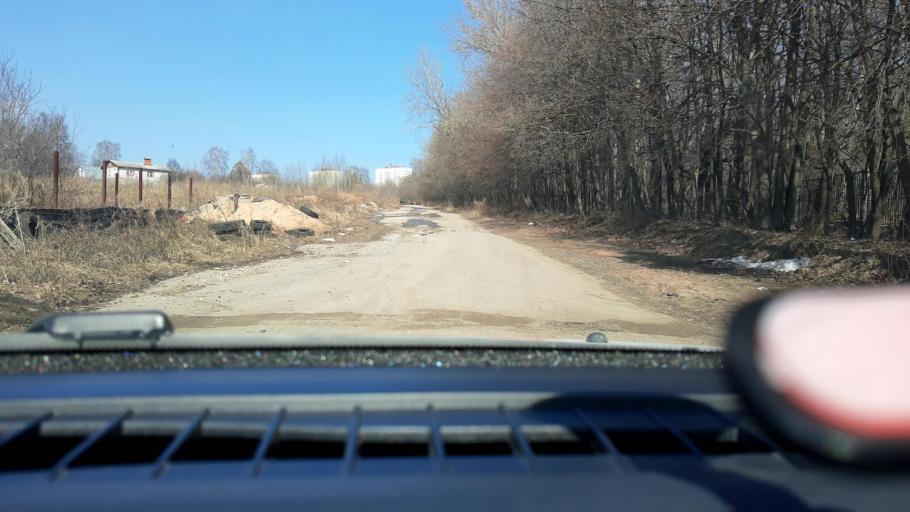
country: RU
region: Nizjnij Novgorod
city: Nizhniy Novgorod
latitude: 56.2531
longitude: 44.0028
